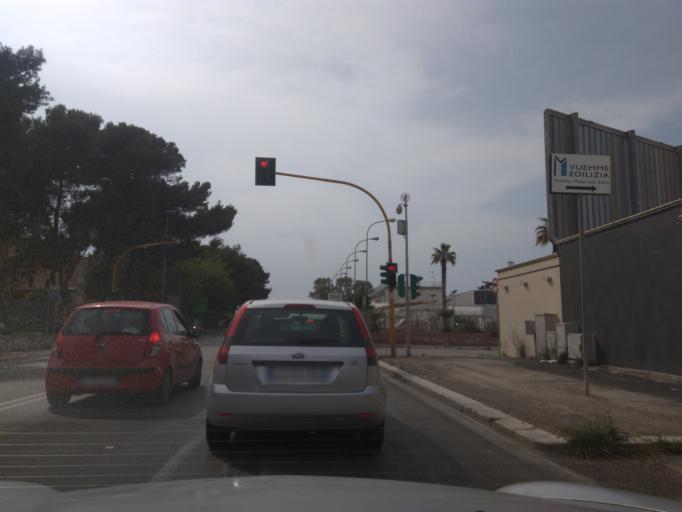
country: IT
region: Apulia
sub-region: Provincia di Bari
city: Bari
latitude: 41.1293
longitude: 16.8342
